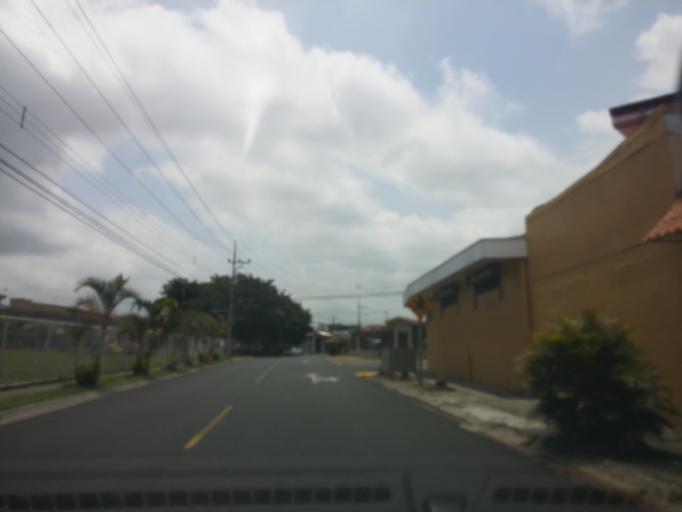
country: CR
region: Heredia
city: San Francisco
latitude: 9.9898
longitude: -84.1294
